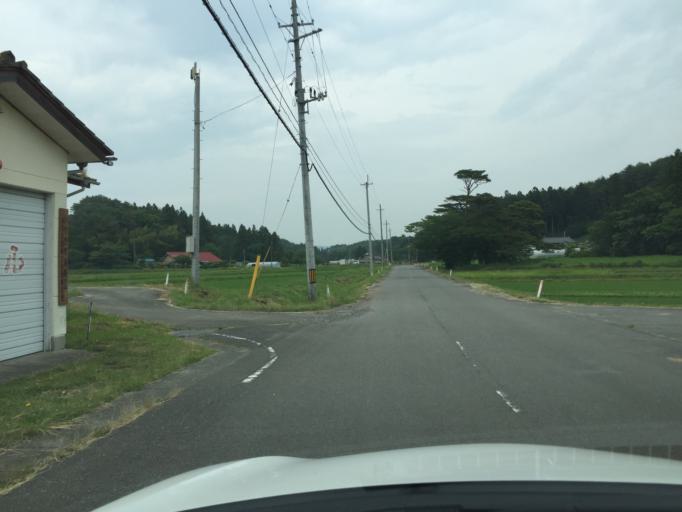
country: JP
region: Fukushima
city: Iwaki
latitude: 37.1957
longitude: 140.7198
